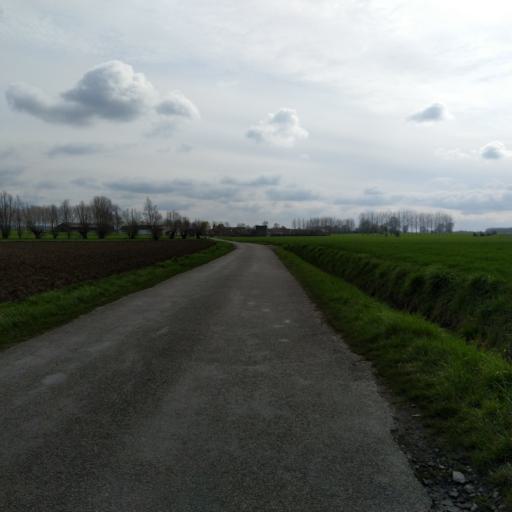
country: BE
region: Wallonia
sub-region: Province du Hainaut
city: Soignies
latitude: 50.5551
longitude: 4.0644
